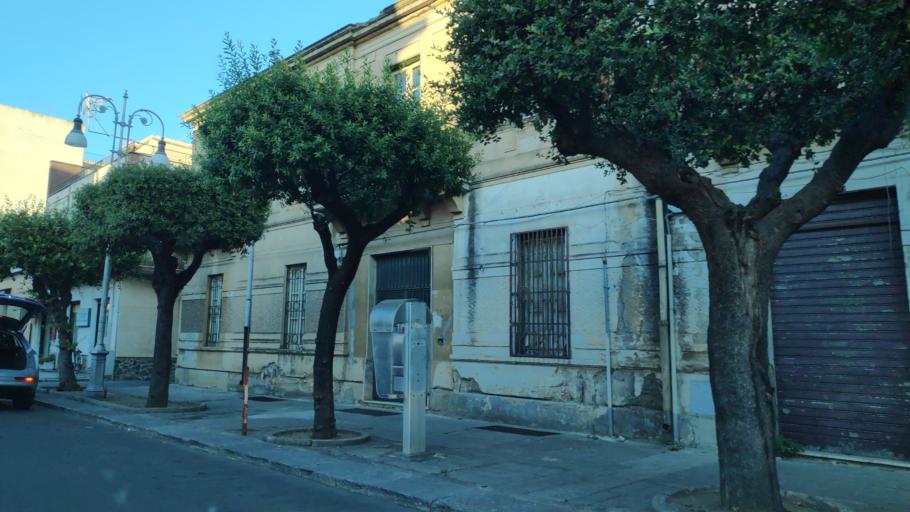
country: IT
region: Calabria
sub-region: Provincia di Reggio Calabria
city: Locri
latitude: 38.2346
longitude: 16.2624
